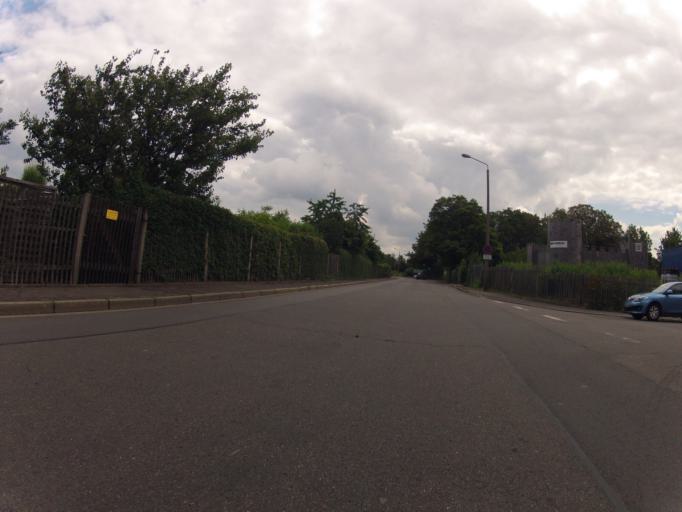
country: DE
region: Saxony
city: Leipzig
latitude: 51.3416
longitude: 12.4319
